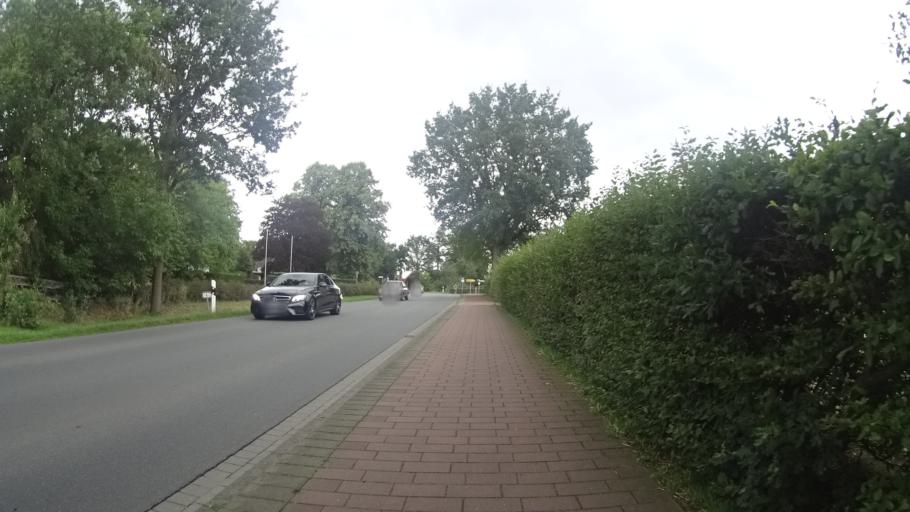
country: DE
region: Lower Saxony
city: Kuhrstedt
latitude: 53.5943
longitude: 8.8111
